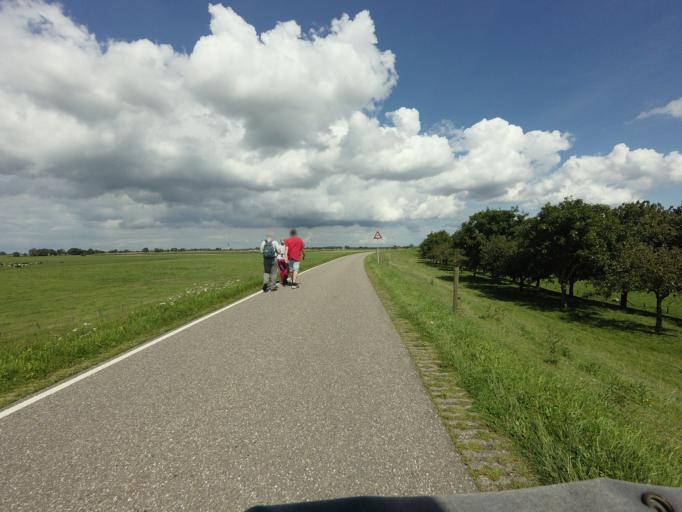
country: NL
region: Utrecht
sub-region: Gemeente IJsselstein
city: IJsselstein
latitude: 51.9728
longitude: 5.0477
